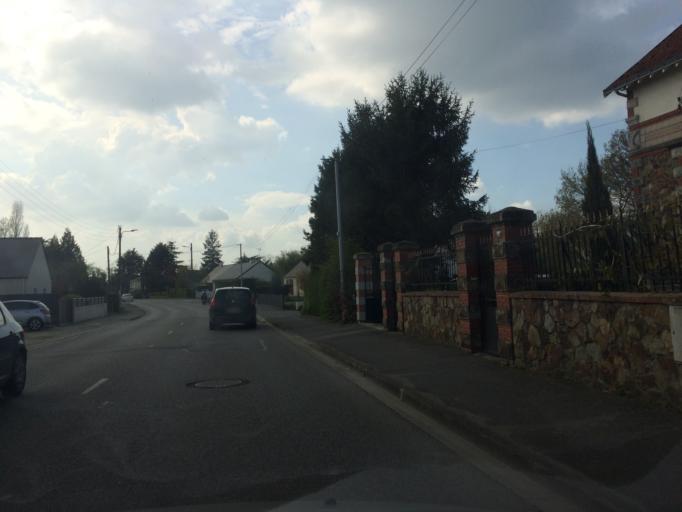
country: FR
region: Pays de la Loire
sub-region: Departement de la Loire-Atlantique
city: Blain
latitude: 47.4783
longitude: -1.7726
